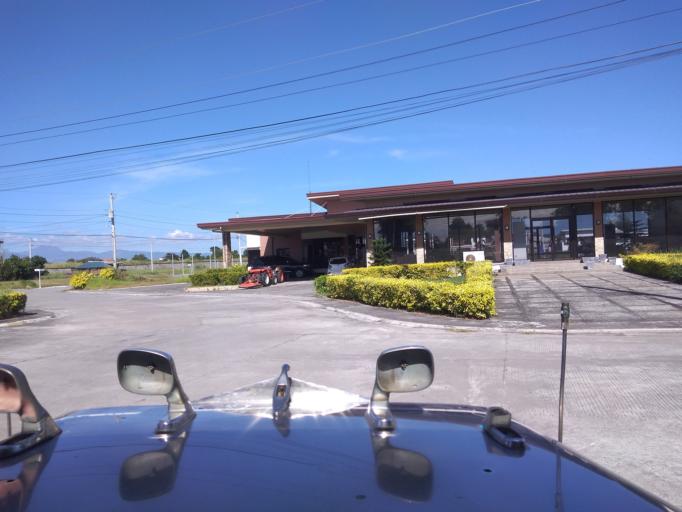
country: PH
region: Central Luzon
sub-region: Province of Pampanga
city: Calibutbut
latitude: 15.1019
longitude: 120.6044
